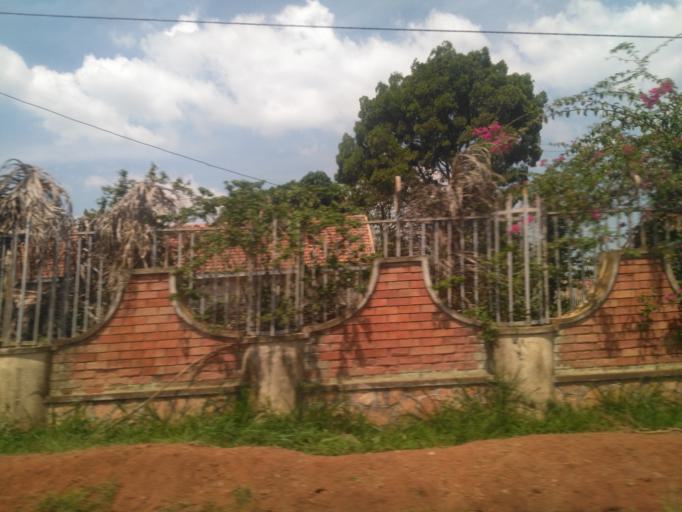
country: UG
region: Central Region
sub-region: Wakiso District
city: Entebbe
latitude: 0.0658
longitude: 32.4748
